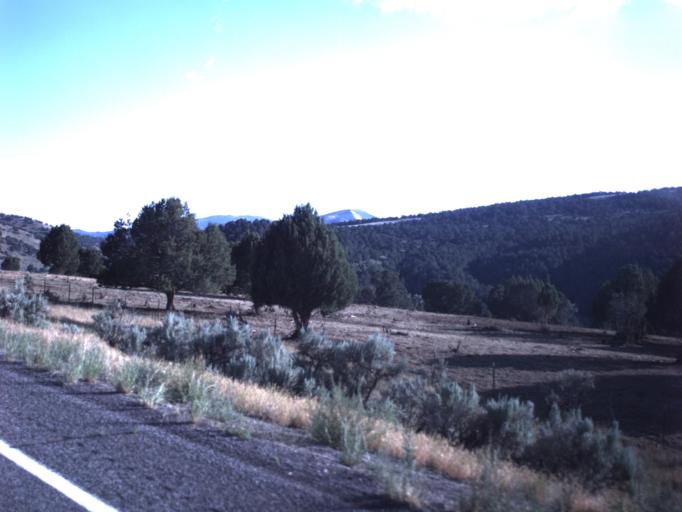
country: US
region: Utah
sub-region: Utah County
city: Woodland Hills
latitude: 39.8953
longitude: -111.5501
